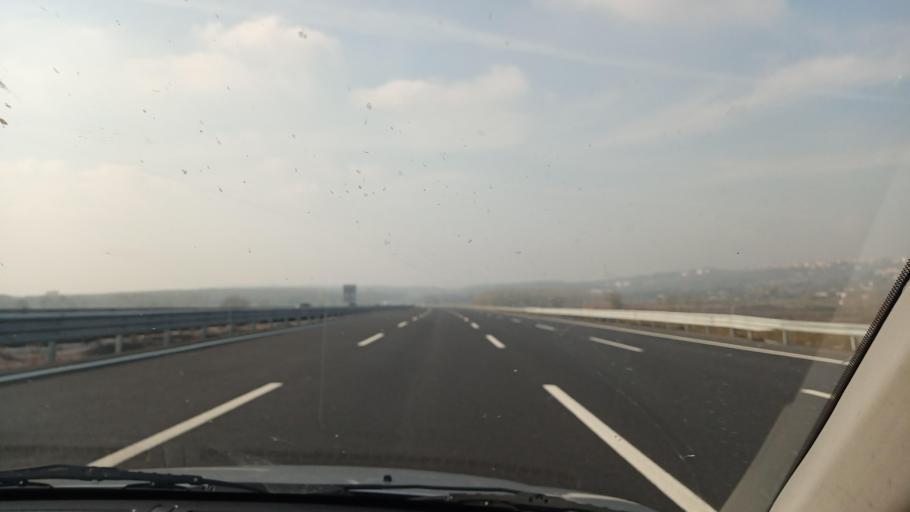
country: TR
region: Sakarya
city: Kazimpasa
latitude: 40.8443
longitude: 30.3260
